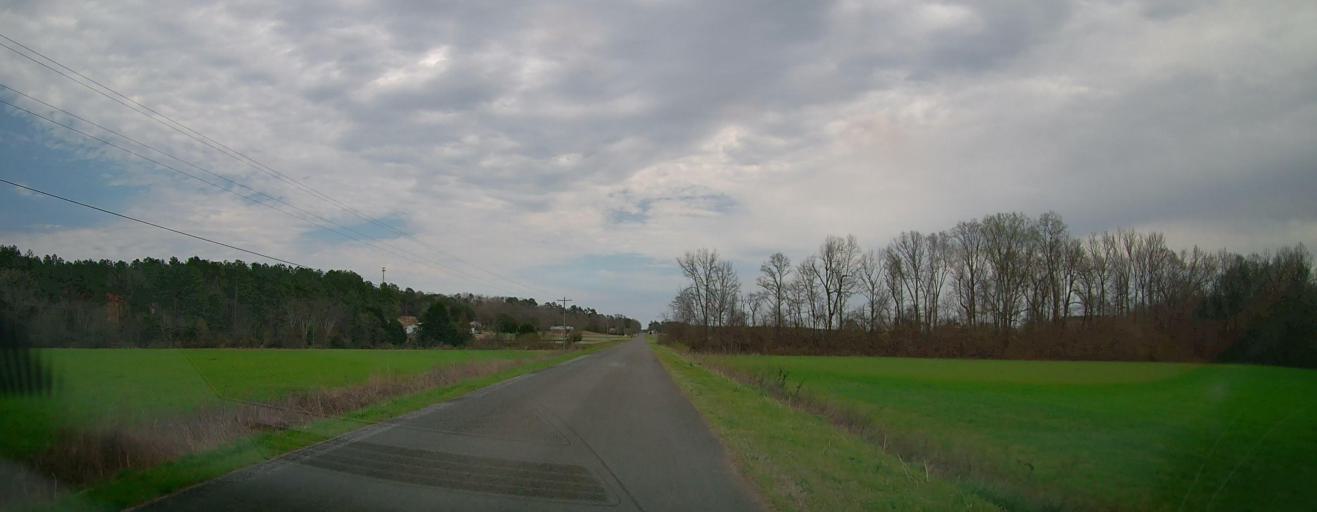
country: US
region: Alabama
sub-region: Marion County
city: Hamilton
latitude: 34.1956
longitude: -88.1603
